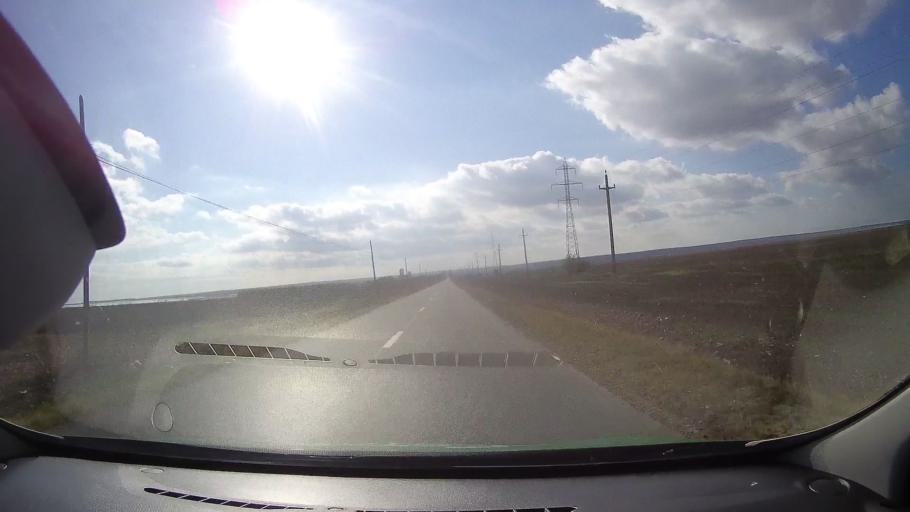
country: RO
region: Constanta
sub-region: Comuna Istria
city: Istria
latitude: 44.5514
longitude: 28.6956
